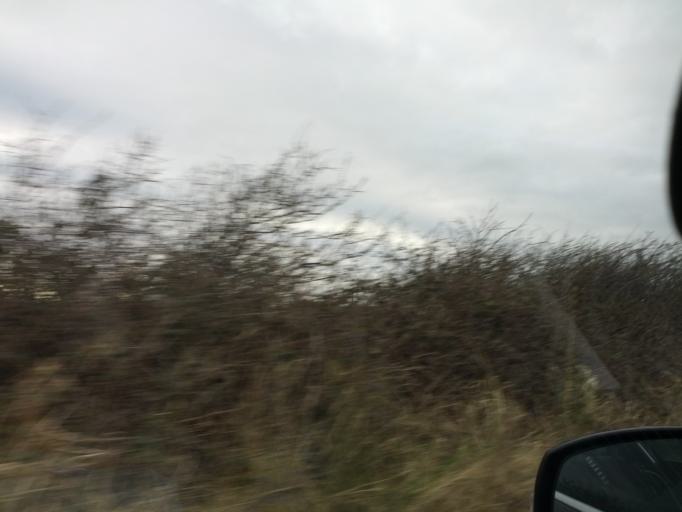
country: IE
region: Connaught
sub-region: County Galway
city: Gort
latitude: 53.1572
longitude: -8.8508
